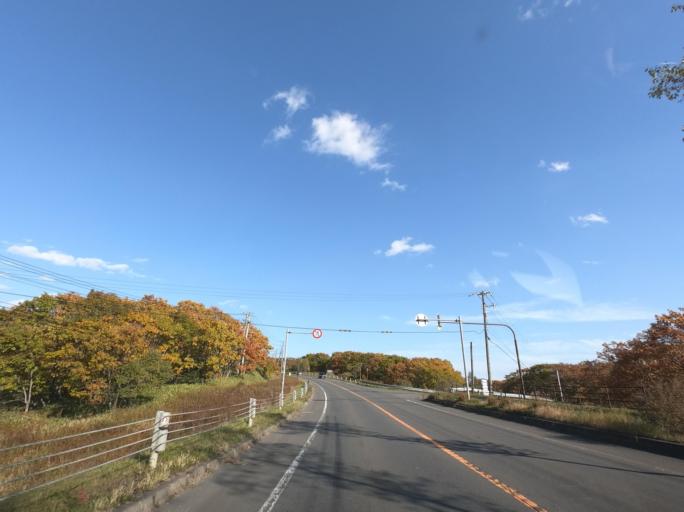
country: JP
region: Hokkaido
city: Kushiro
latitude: 43.0684
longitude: 144.3142
